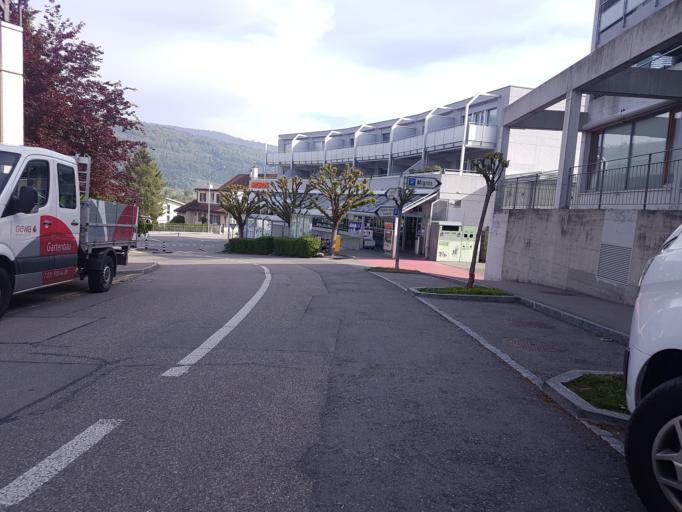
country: CH
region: Bern
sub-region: Biel/Bienne District
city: Nidau
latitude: 47.1152
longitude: 7.2350
